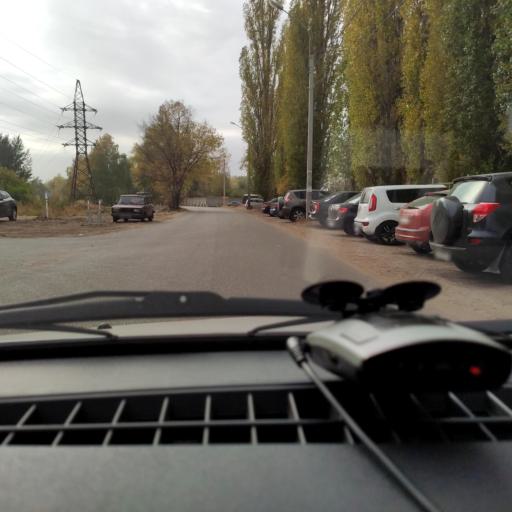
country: RU
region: Voronezj
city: Podgornoye
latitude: 51.7436
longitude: 39.1747
